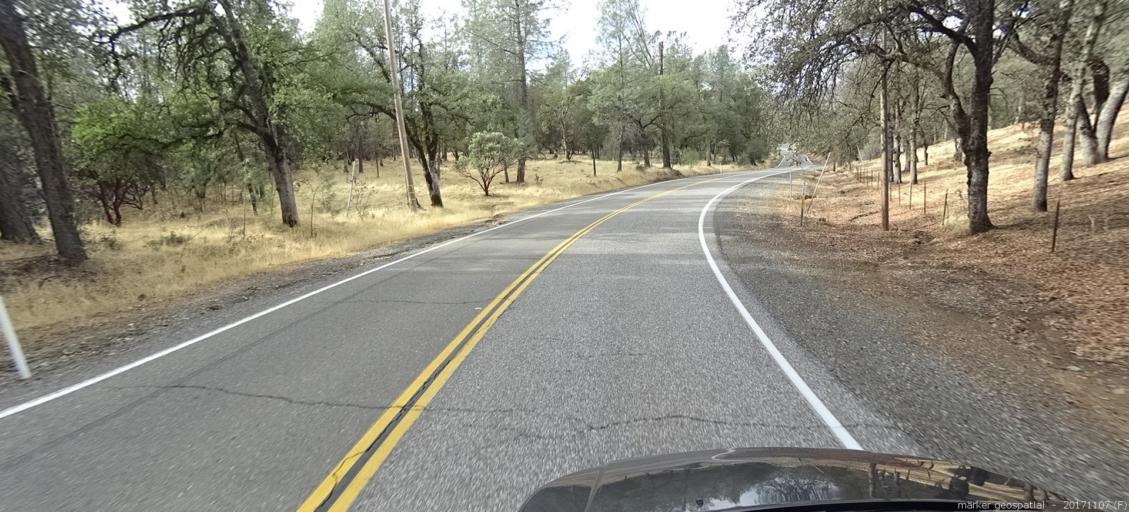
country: US
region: California
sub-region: Shasta County
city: Shasta
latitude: 40.5158
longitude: -122.5071
